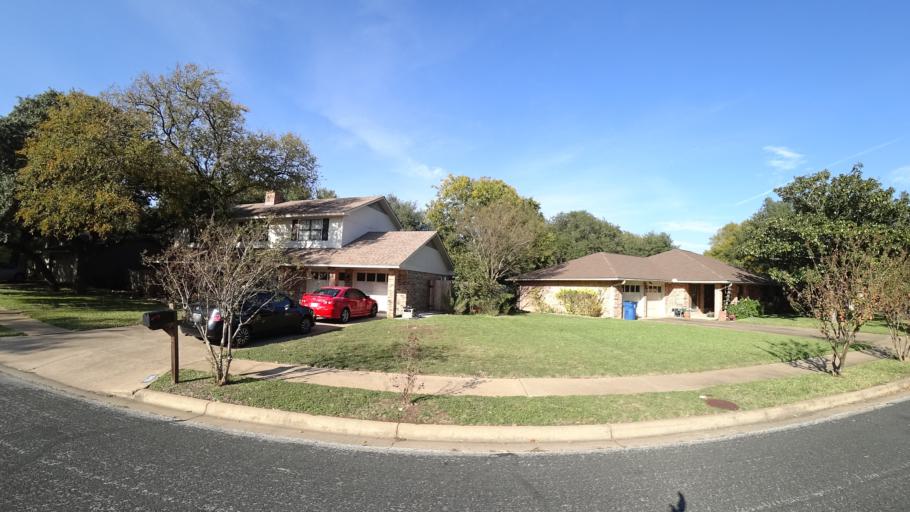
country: US
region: Texas
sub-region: Williamson County
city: Anderson Mill
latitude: 30.4488
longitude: -97.8062
